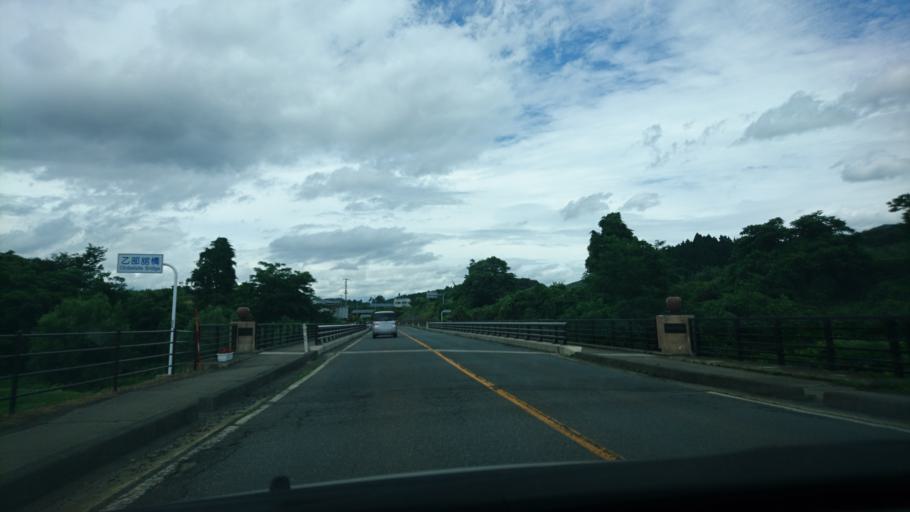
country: JP
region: Iwate
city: Morioka-shi
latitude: 39.6092
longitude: 141.2032
